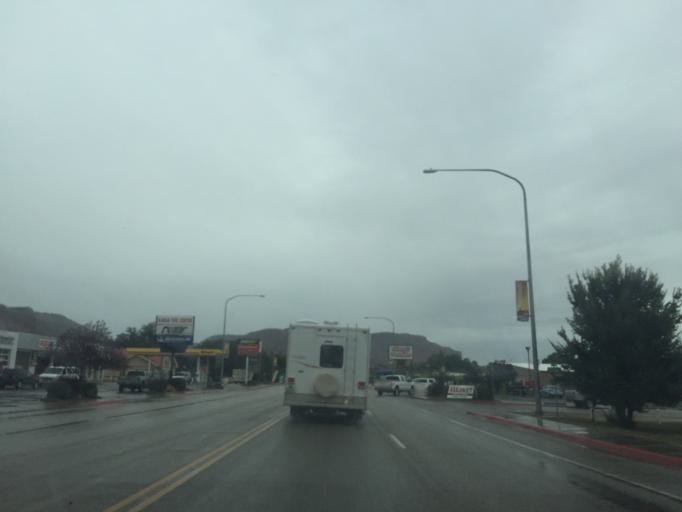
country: US
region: Utah
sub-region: Kane County
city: Kanab
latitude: 37.0430
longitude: -112.5238
